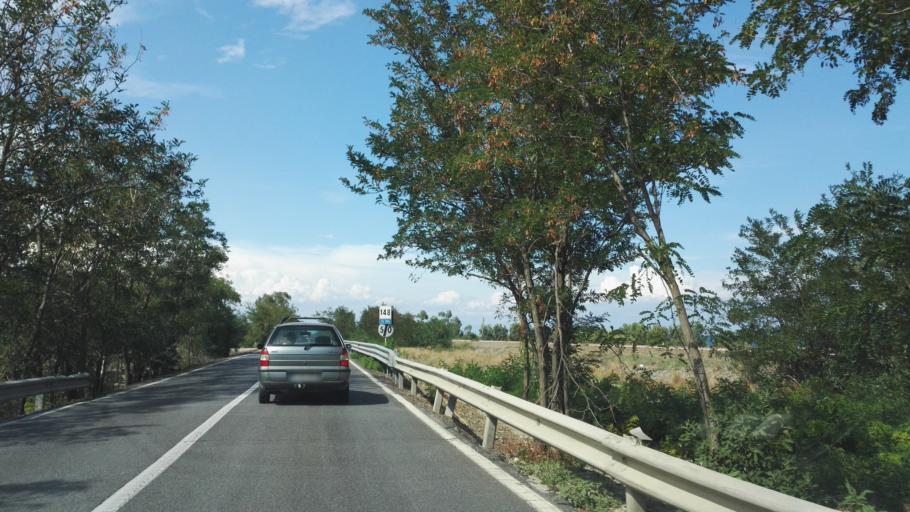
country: IT
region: Calabria
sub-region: Provincia di Catanzaro
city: Santa Caterina dello Ionio Marina
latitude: 38.5477
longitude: 16.5701
